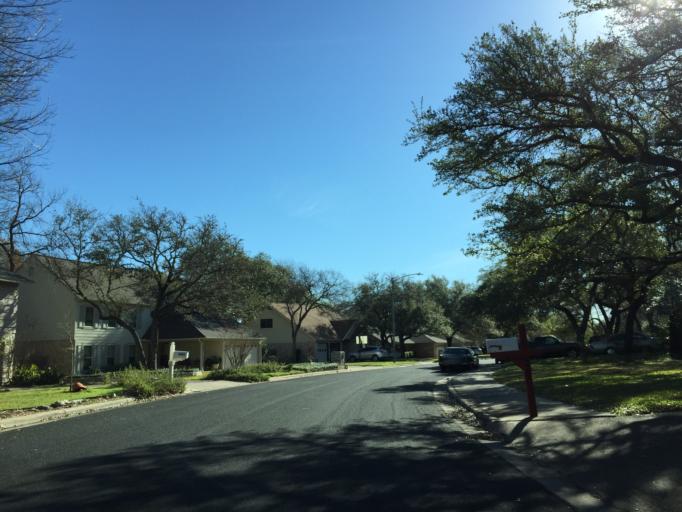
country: US
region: Texas
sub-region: Williamson County
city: Jollyville
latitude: 30.4078
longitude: -97.7358
